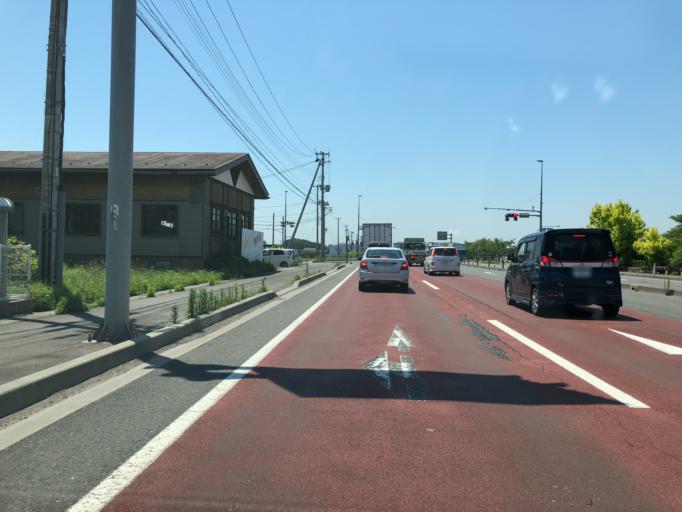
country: JP
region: Fukushima
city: Motomiya
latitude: 37.5400
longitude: 140.3972
